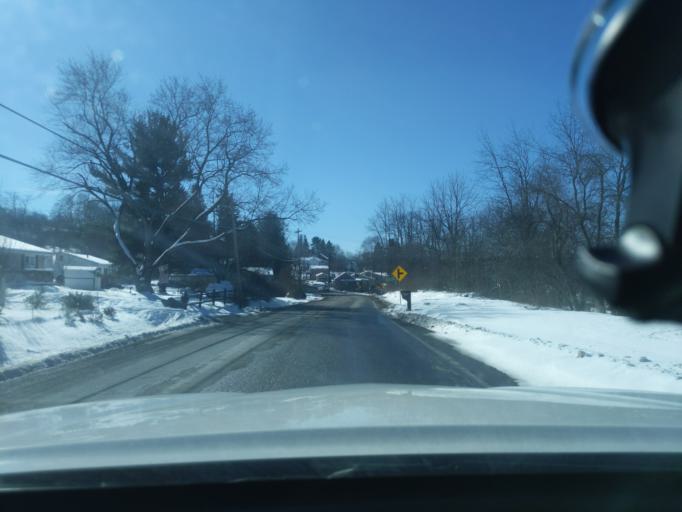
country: US
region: Maryland
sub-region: Allegany County
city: Frostburg
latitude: 39.6282
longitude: -78.9364
